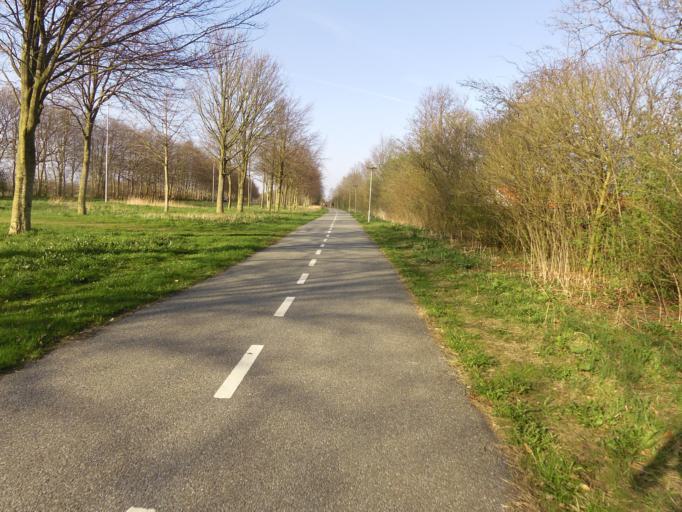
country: DK
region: South Denmark
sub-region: Vejen Kommune
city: Vejen
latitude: 55.4642
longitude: 9.1175
